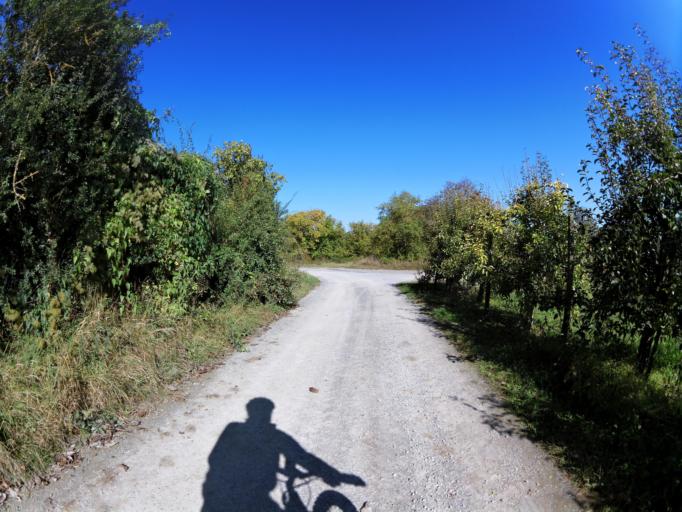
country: DE
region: Bavaria
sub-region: Regierungsbezirk Unterfranken
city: Sommerhausen
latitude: 49.6964
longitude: 10.0414
